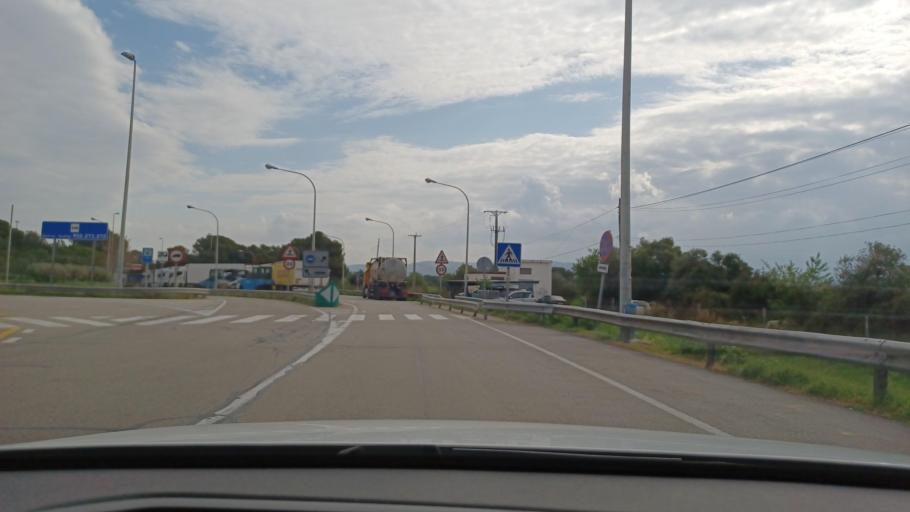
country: ES
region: Catalonia
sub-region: Provincia de Tarragona
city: Sant Jaume dels Domenys
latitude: 41.2879
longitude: 1.5917
